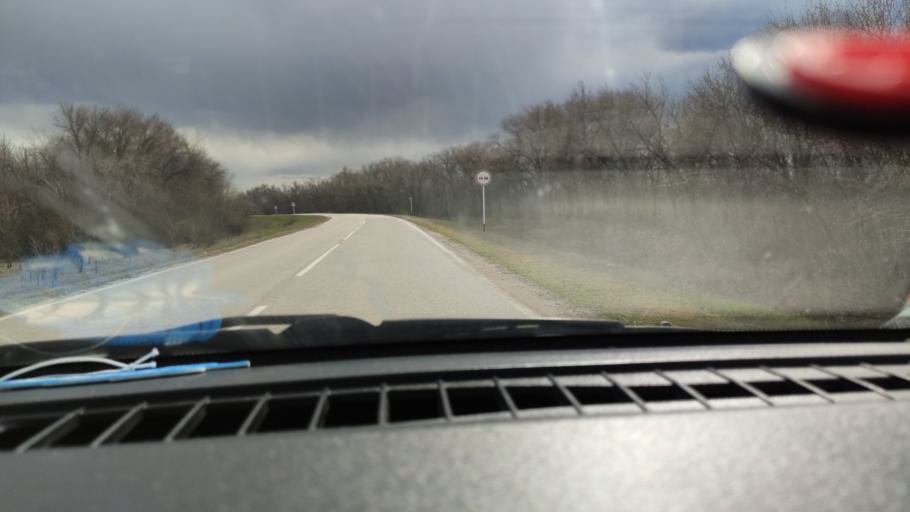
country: RU
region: Saratov
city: Privolzhskiy
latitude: 51.2690
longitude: 45.9468
